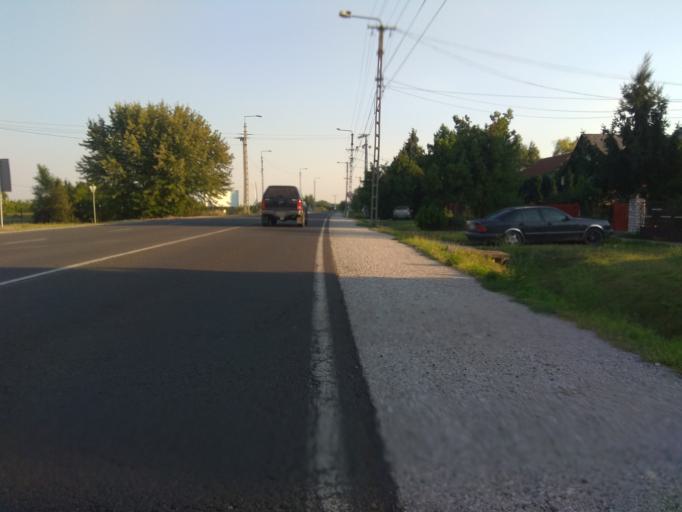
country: HU
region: Borsod-Abauj-Zemplen
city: Nyekladhaza
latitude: 47.9854
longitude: 20.8313
